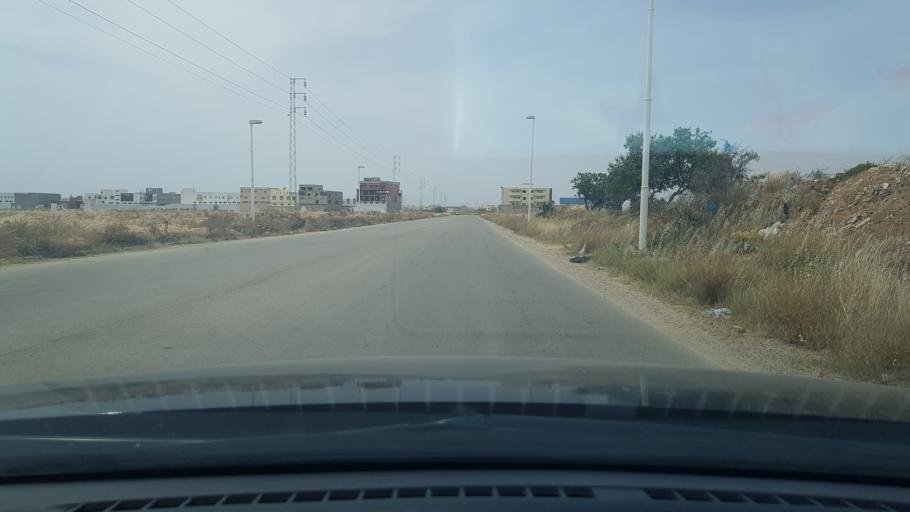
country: TN
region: Safaqis
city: Al Qarmadah
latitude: 34.8307
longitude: 10.7422
